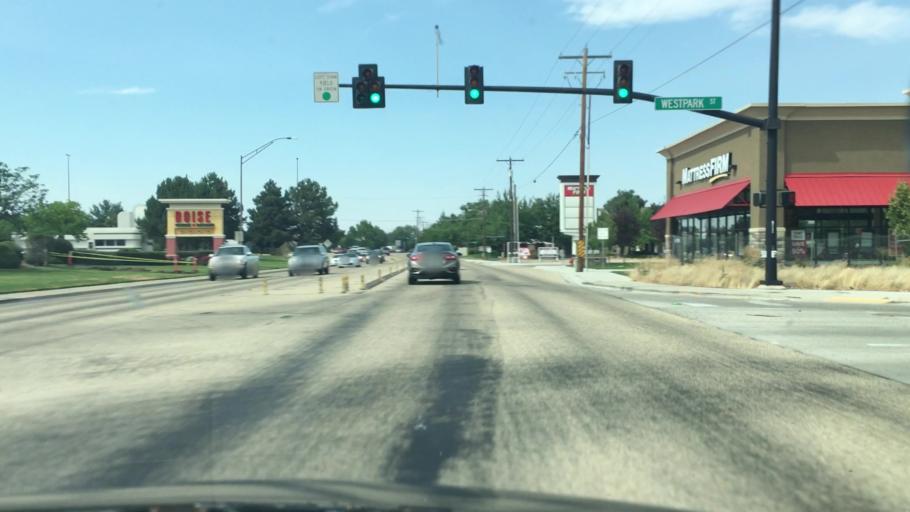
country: US
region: Idaho
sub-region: Ada County
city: Garden City
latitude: 43.6090
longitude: -116.2739
